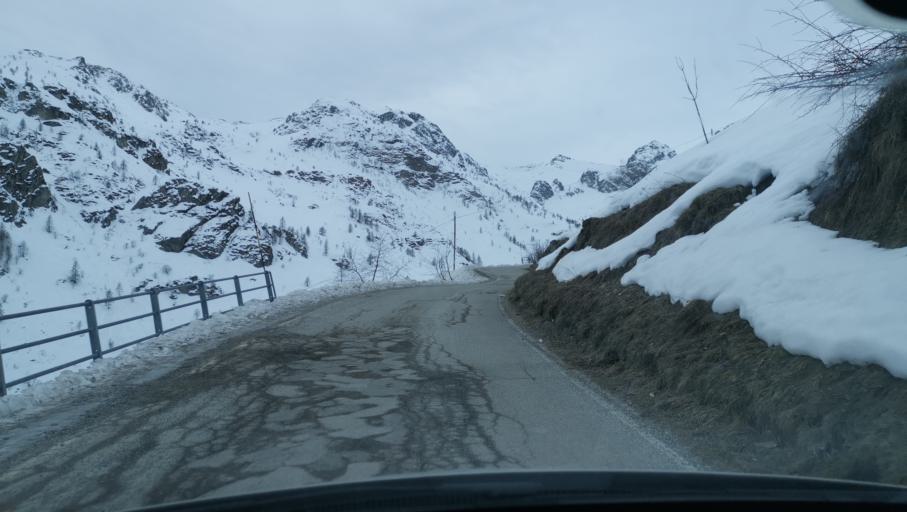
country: IT
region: Piedmont
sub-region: Provincia di Cuneo
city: Campomolino
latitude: 44.4001
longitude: 7.1726
